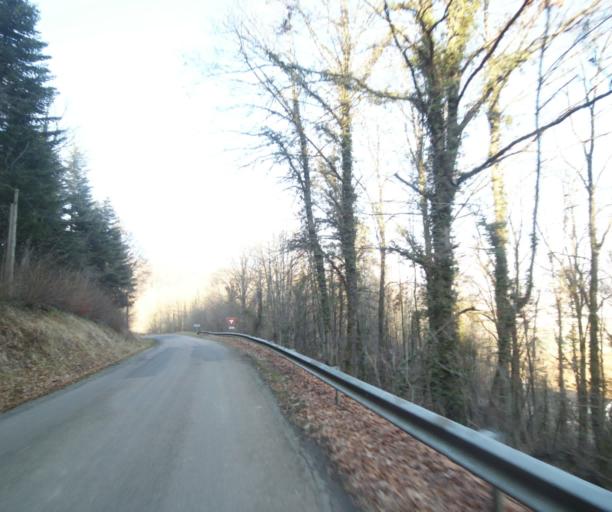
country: FR
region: Champagne-Ardenne
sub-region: Departement de la Haute-Marne
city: Chevillon
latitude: 48.5223
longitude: 5.0912
